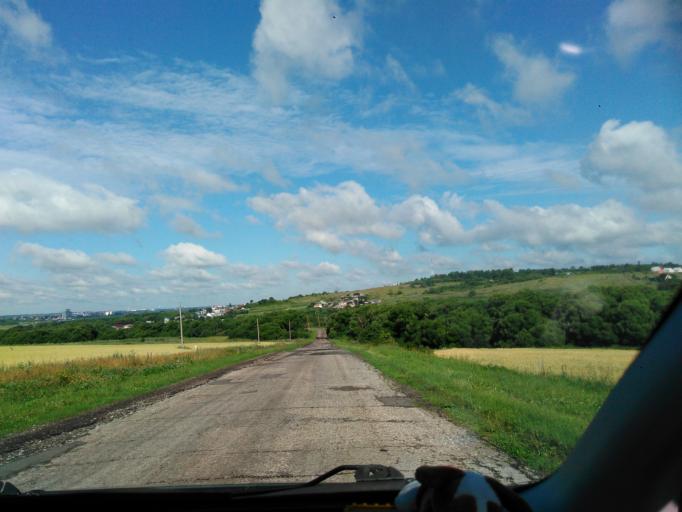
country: RU
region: Penza
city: Lermontovo
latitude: 53.1788
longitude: 44.0941
